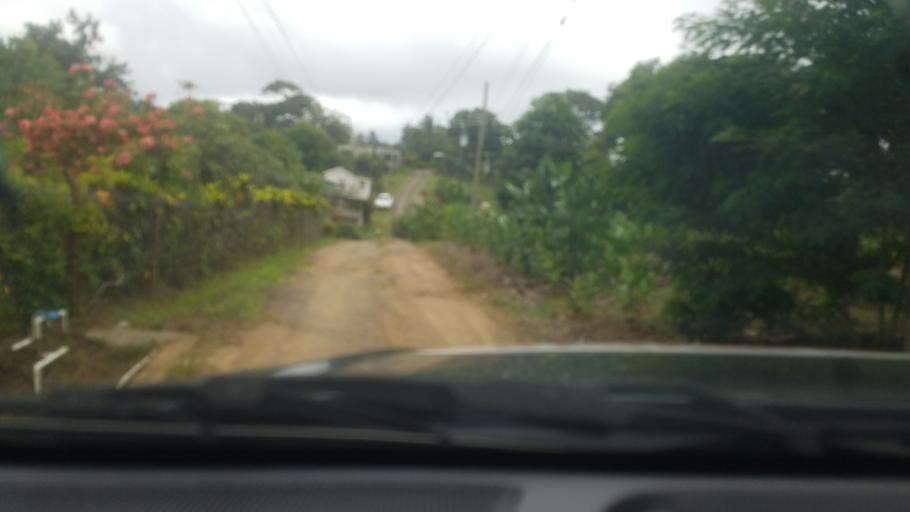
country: LC
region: Micoud Quarter
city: Micoud
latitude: 13.8042
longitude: -60.9411
